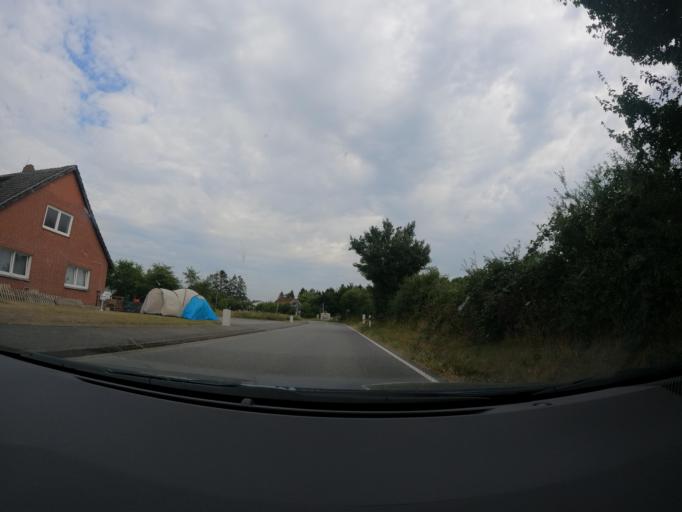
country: DE
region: Schleswig-Holstein
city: Selk
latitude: 54.4770
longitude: 9.5469
